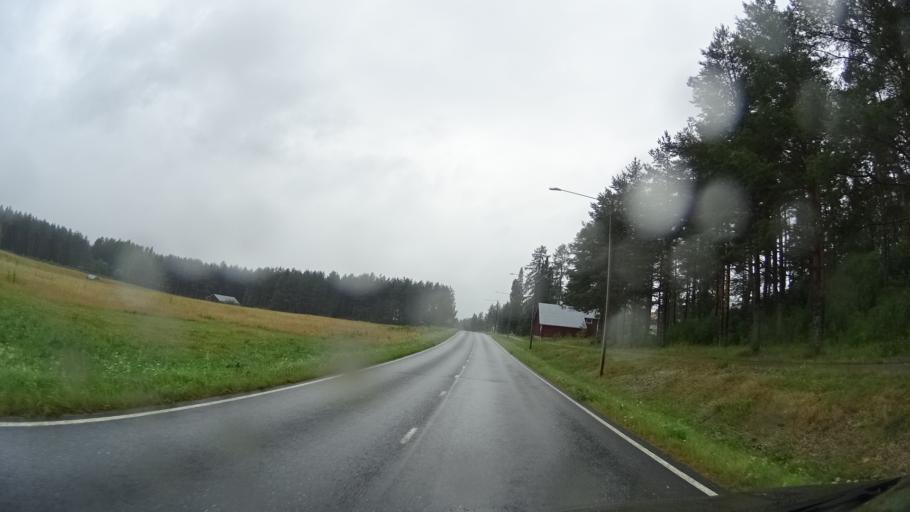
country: FI
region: North Karelia
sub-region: Keski-Karjala
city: Raeaekkylae
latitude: 62.3159
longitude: 29.6177
